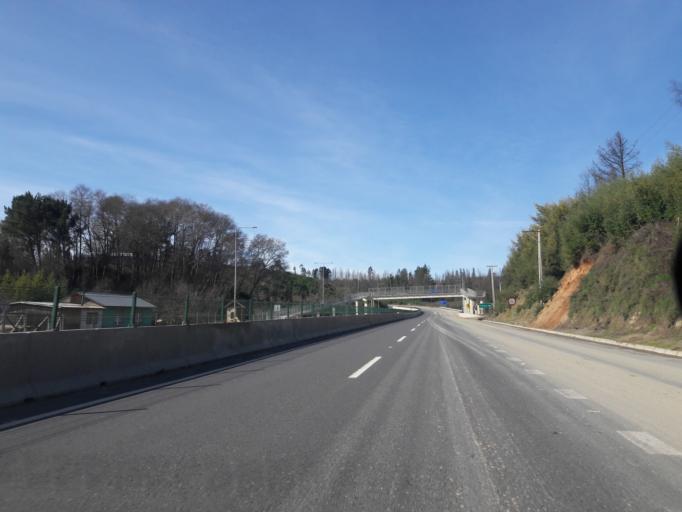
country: CL
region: Biobio
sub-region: Provincia de Concepcion
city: Chiguayante
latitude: -36.8638
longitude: -72.8553
